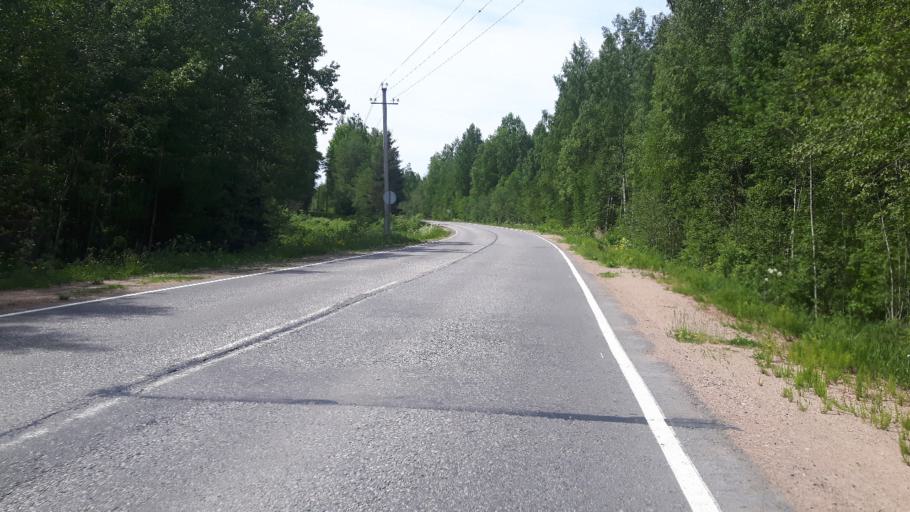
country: RU
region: Leningrad
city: Ust'-Luga
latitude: 59.6468
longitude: 28.2031
